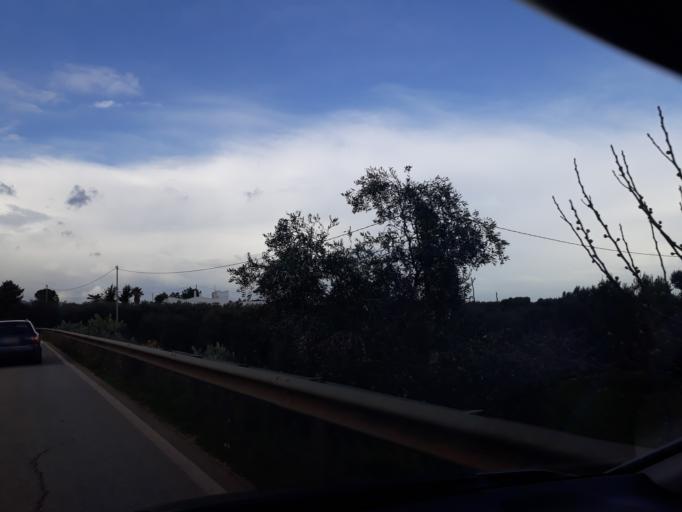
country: IT
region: Apulia
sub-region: Provincia di Brindisi
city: Pezze di Greco
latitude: 40.8011
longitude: 17.4011
